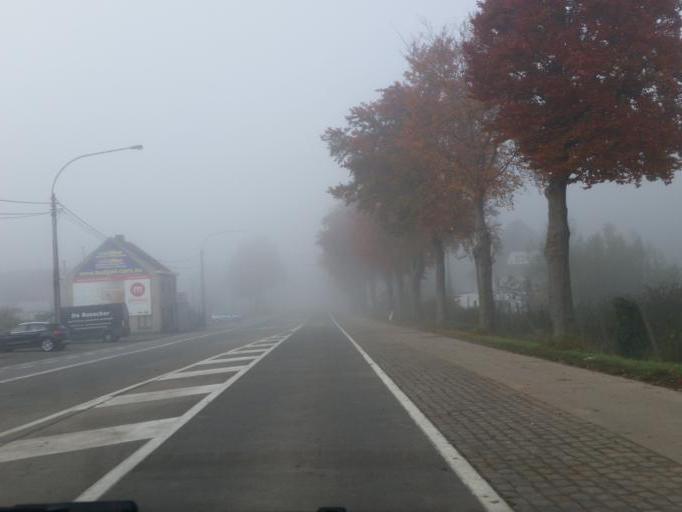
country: BE
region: Flanders
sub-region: Provincie Oost-Vlaanderen
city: Lede
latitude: 50.9465
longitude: 3.9580
